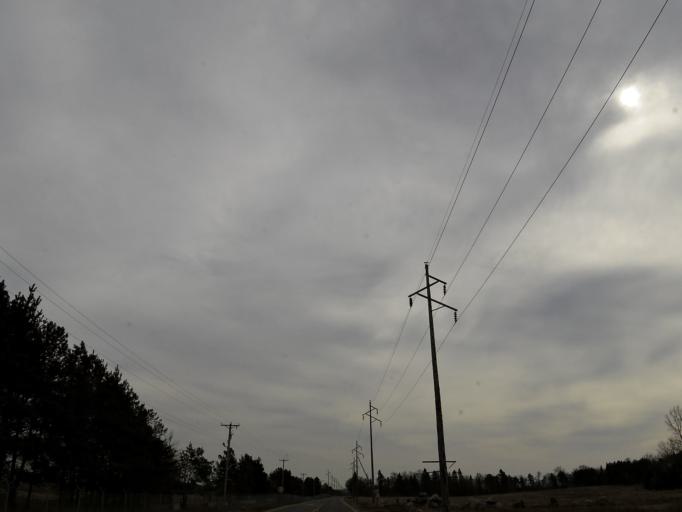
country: US
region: Minnesota
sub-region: Dakota County
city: Rosemount
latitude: 44.7723
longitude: -93.0592
